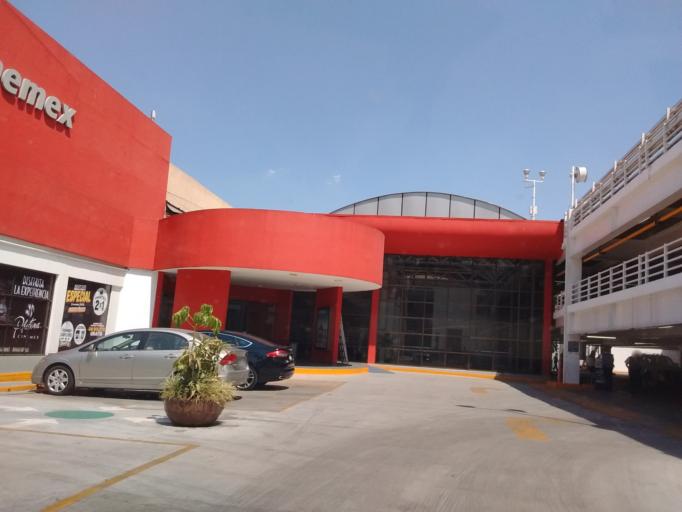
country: MX
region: Mexico City
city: Miguel Hidalgo
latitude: 19.4375
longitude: -99.2077
